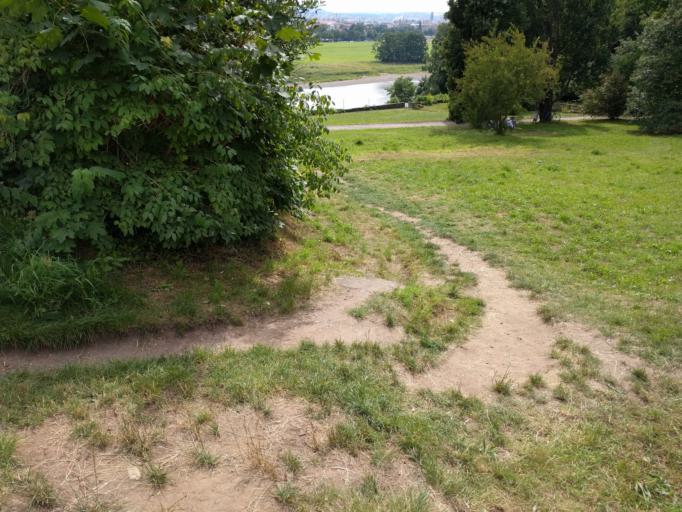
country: DE
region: Saxony
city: Albertstadt
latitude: 51.0650
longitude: 13.7921
